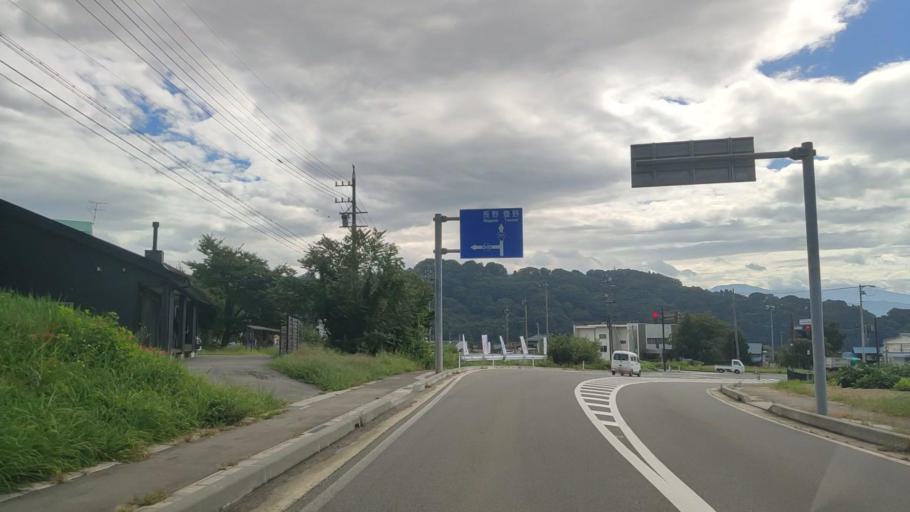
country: JP
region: Nagano
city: Nakano
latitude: 36.7745
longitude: 138.3256
